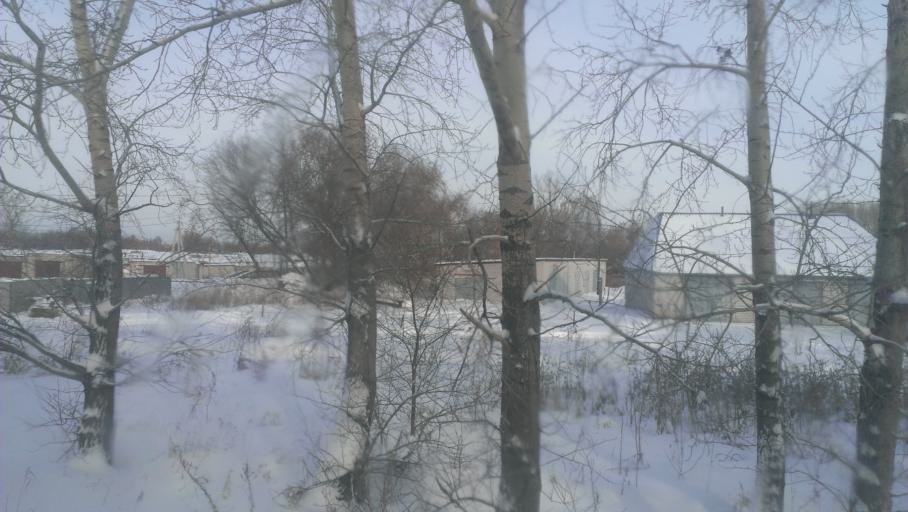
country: RU
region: Altai Krai
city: Nauchnyy Gorodok
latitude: 53.4209
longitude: 83.5227
